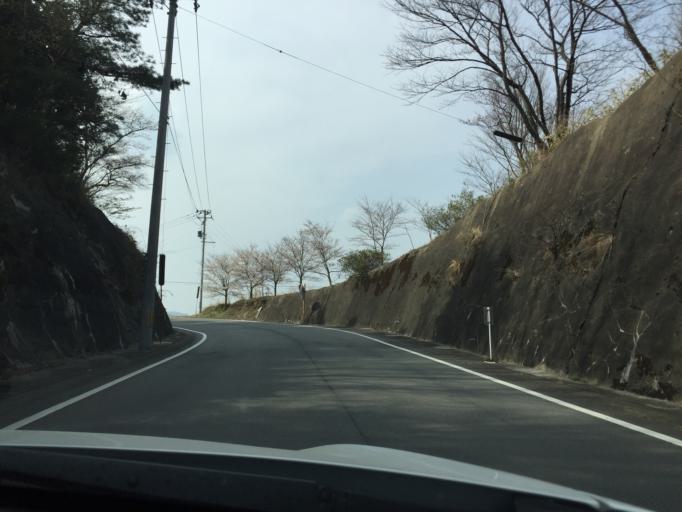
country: JP
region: Fukushima
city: Iwaki
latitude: 37.0318
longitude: 140.7220
